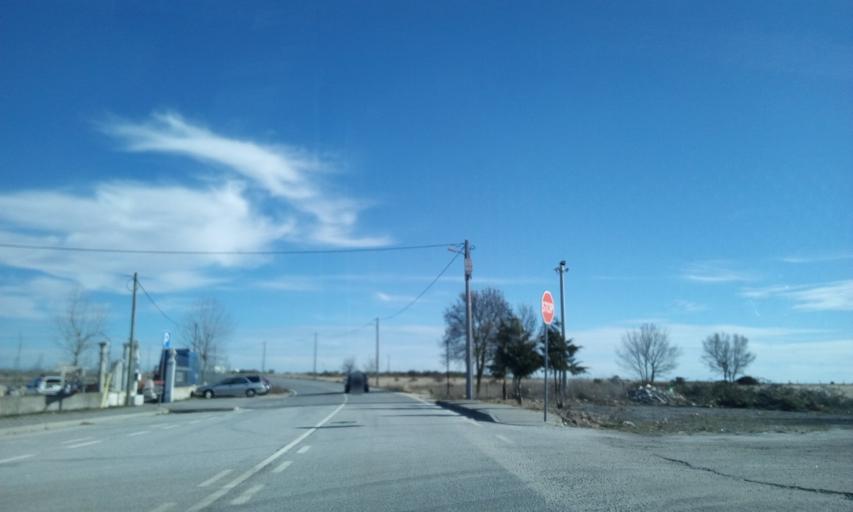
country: ES
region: Castille and Leon
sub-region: Provincia de Salamanca
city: Fuentes de Onoro
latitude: 40.5937
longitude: -6.9911
